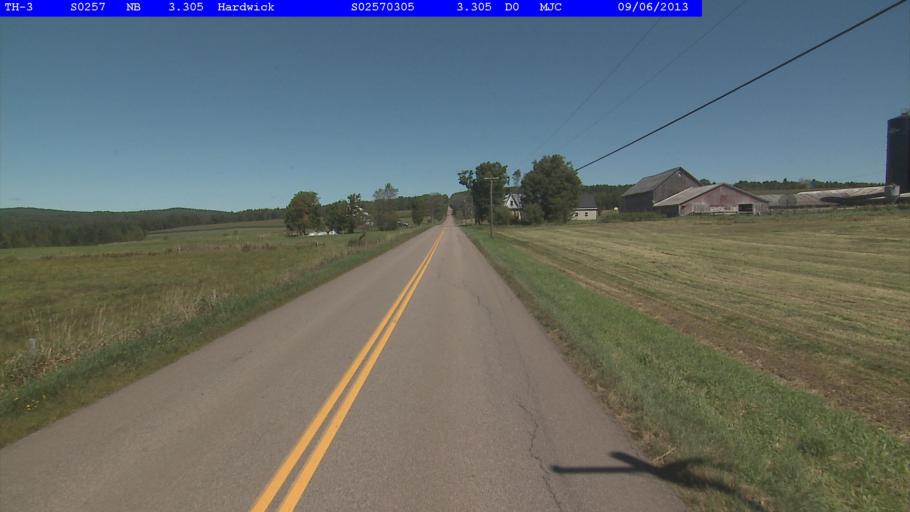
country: US
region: Vermont
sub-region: Caledonia County
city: Hardwick
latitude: 44.5370
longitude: -72.3305
